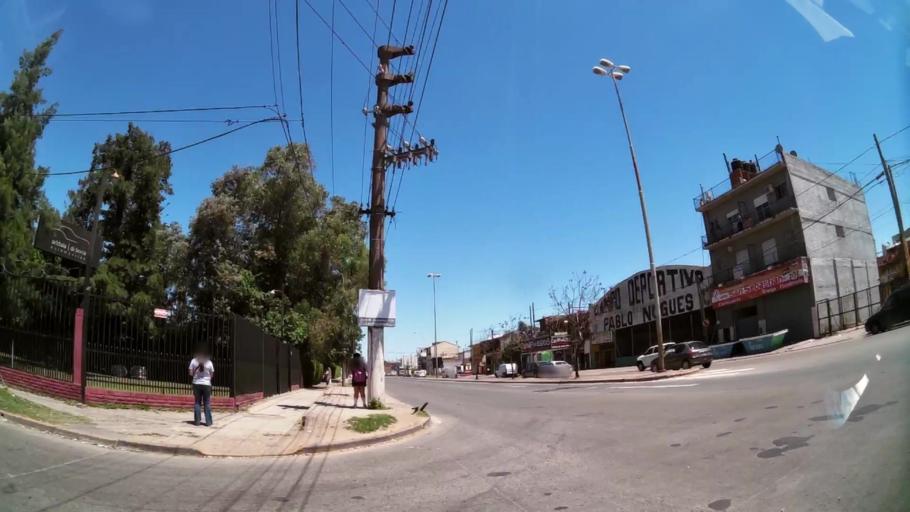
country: AR
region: Buenos Aires
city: Hurlingham
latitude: -34.5041
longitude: -58.7171
